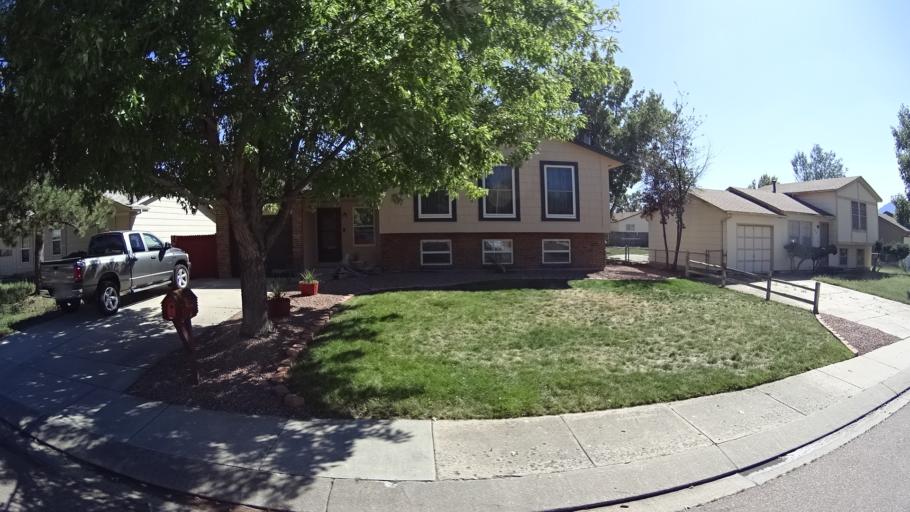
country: US
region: Colorado
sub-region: El Paso County
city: Stratmoor
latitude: 38.7938
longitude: -104.7451
